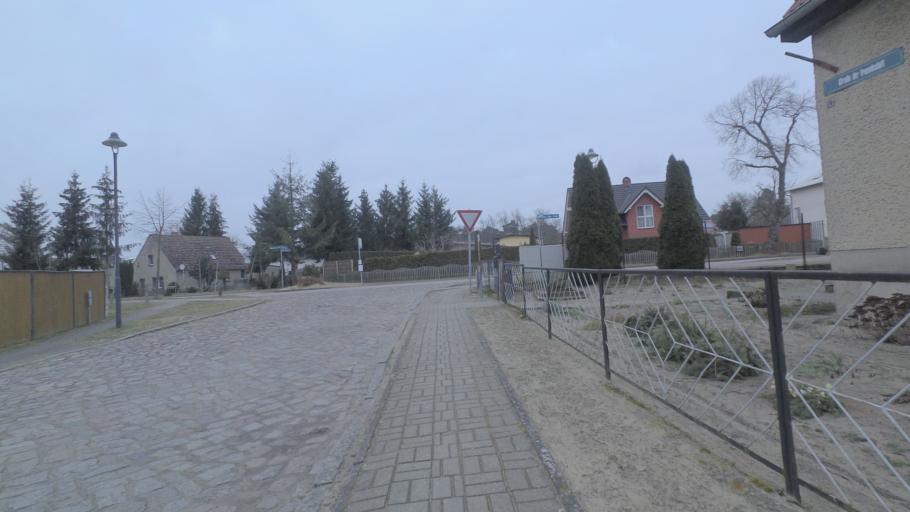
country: DE
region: Brandenburg
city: Stahnsdorf
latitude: 52.3386
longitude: 13.2251
